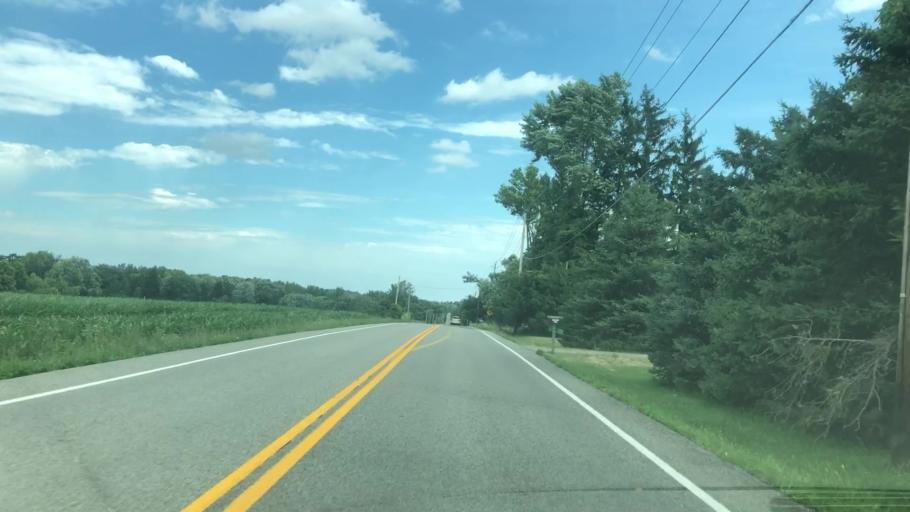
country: US
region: New York
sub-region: Wayne County
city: Macedon
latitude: 43.1029
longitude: -77.3522
